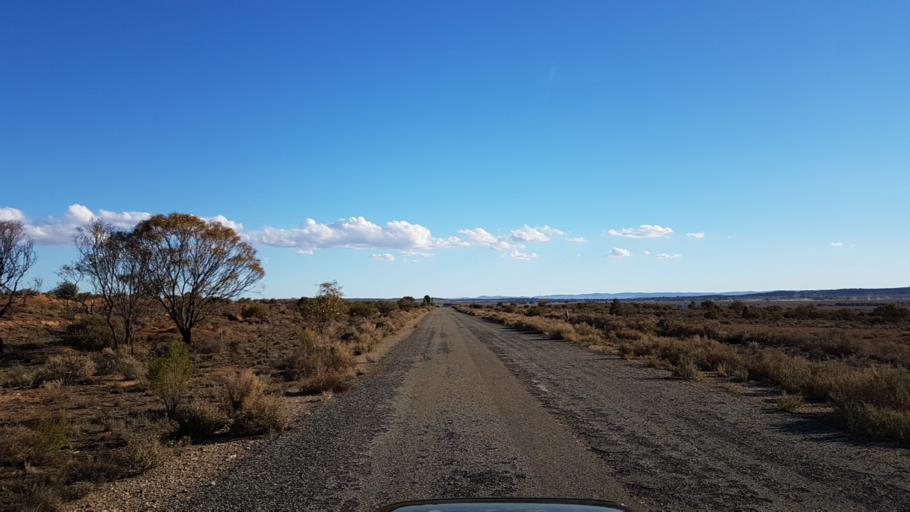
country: AU
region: South Australia
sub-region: Peterborough
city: Peterborough
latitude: -32.9562
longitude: 138.9004
